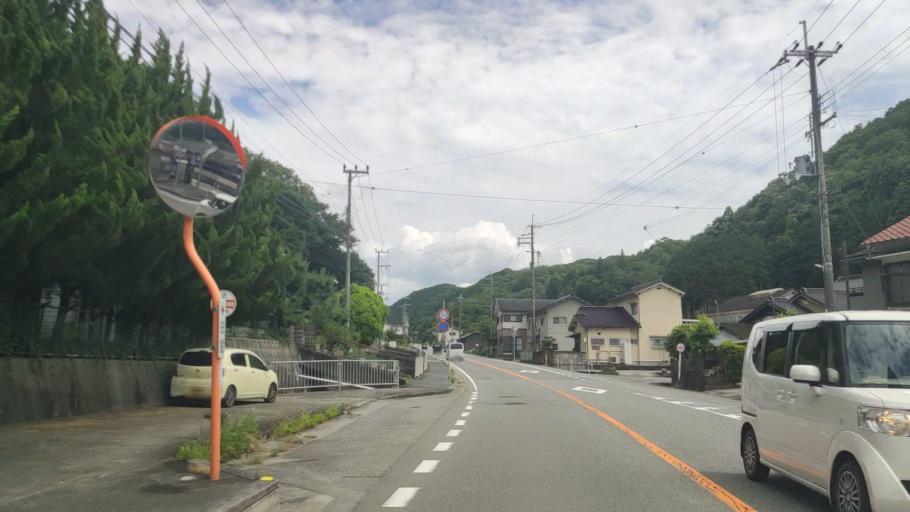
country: JP
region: Hyogo
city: Yamazakicho-nakabirose
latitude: 35.0054
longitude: 134.3643
